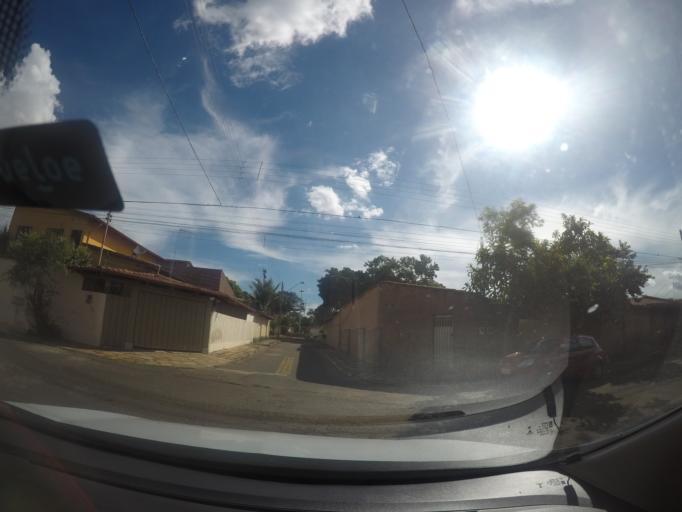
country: BR
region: Goias
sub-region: Goiania
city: Goiania
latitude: -16.6795
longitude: -49.2994
